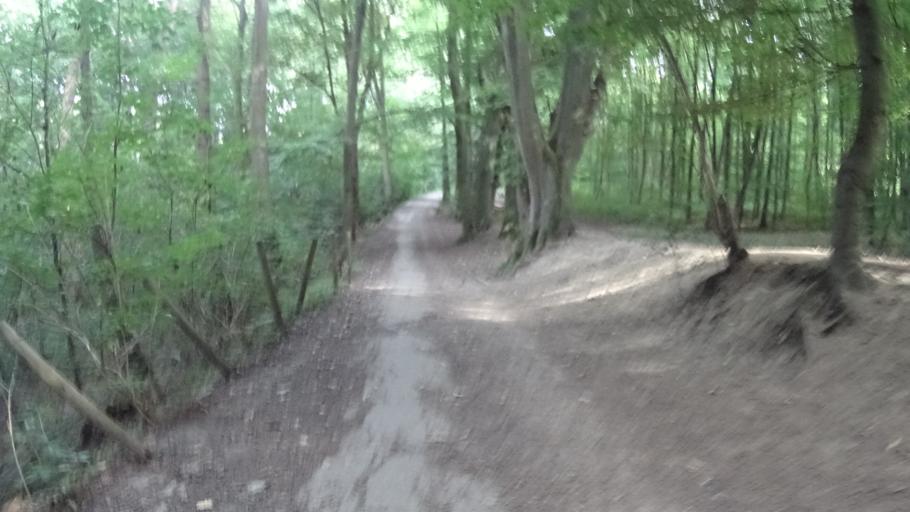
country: DE
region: North Rhine-Westphalia
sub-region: Regierungsbezirk Arnsberg
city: Dortmund
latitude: 51.4869
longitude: 7.4525
